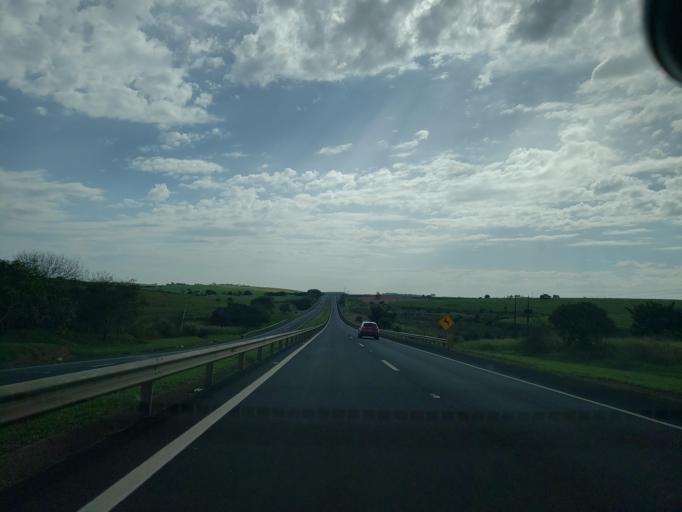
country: BR
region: Sao Paulo
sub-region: Lins
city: Lins
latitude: -21.7446
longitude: -49.6937
